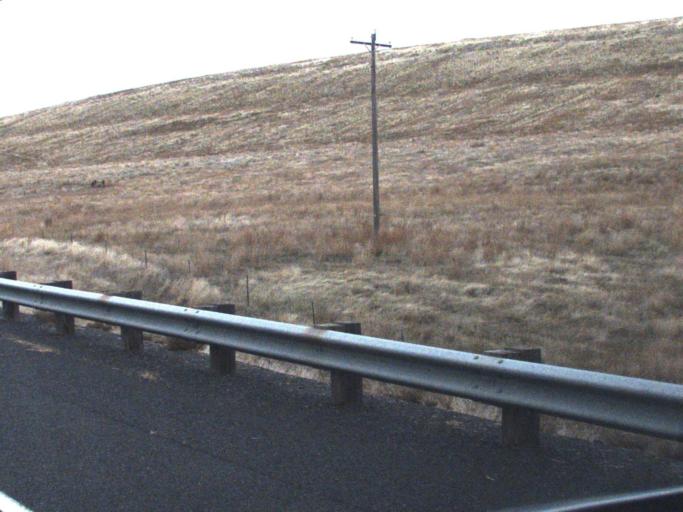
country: US
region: Washington
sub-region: Adams County
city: Ritzville
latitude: 46.7777
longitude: -118.0802
